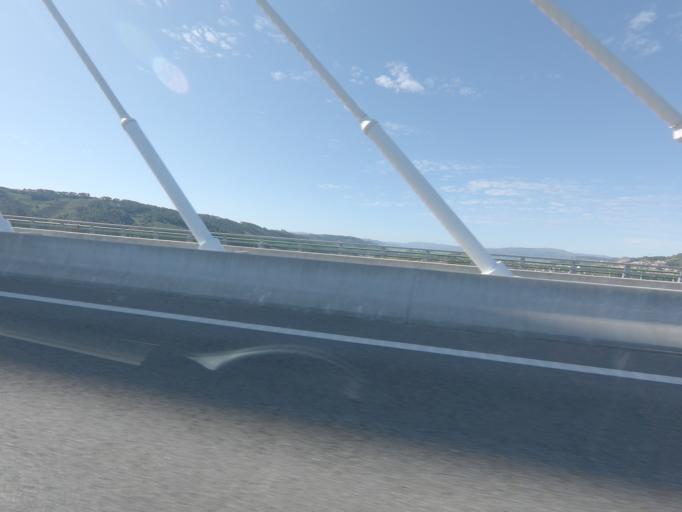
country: PT
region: Vila Real
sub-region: Vila Real
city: Vila Real
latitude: 41.2784
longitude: -7.7528
